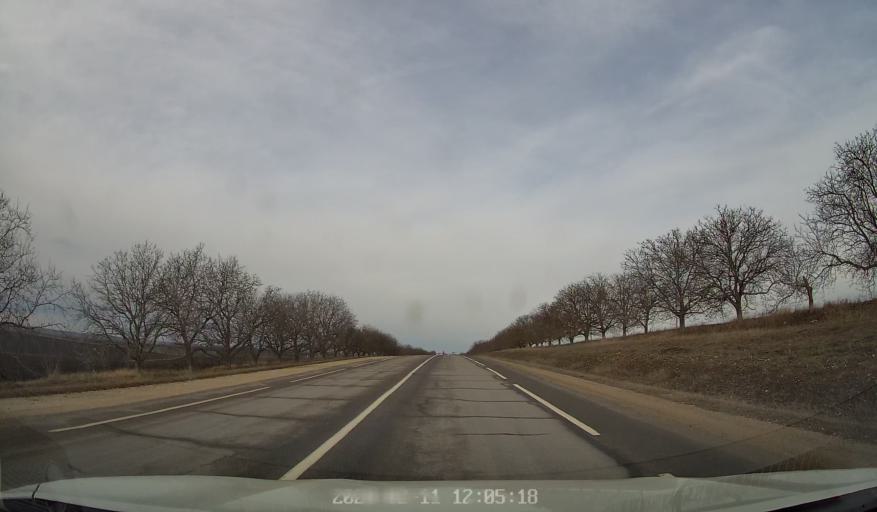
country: MD
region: Riscani
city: Riscani
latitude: 47.9799
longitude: 27.5836
